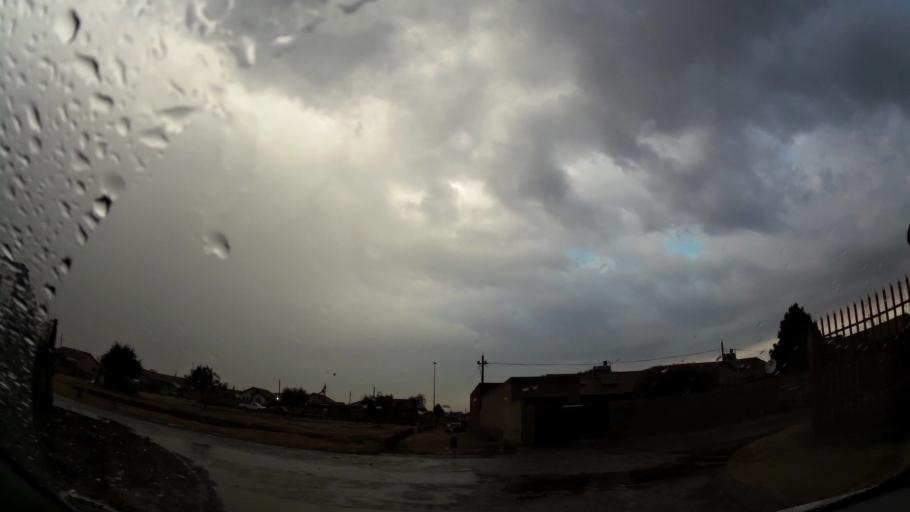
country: ZA
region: Gauteng
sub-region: Ekurhuleni Metropolitan Municipality
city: Germiston
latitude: -26.3618
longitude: 28.1301
